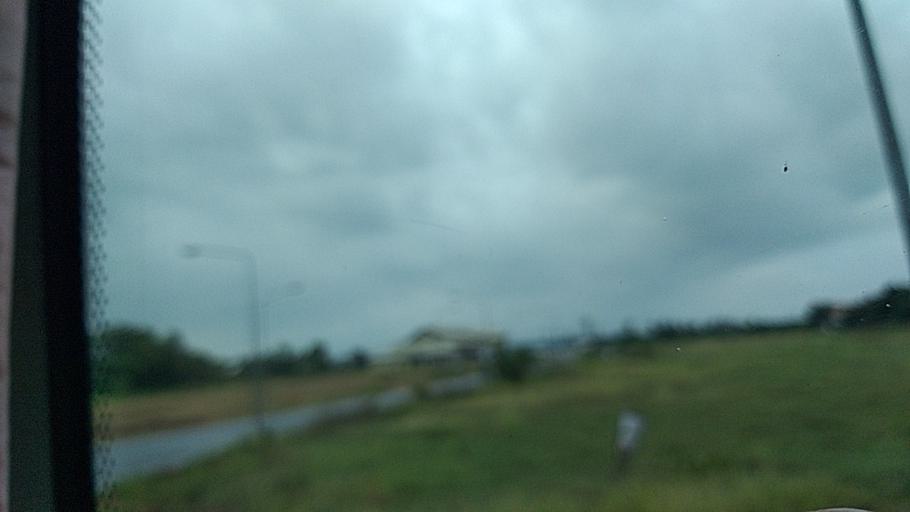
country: TH
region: Maha Sarakham
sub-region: Amphoe Borabue
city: Borabue
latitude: 16.0394
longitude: 103.1265
